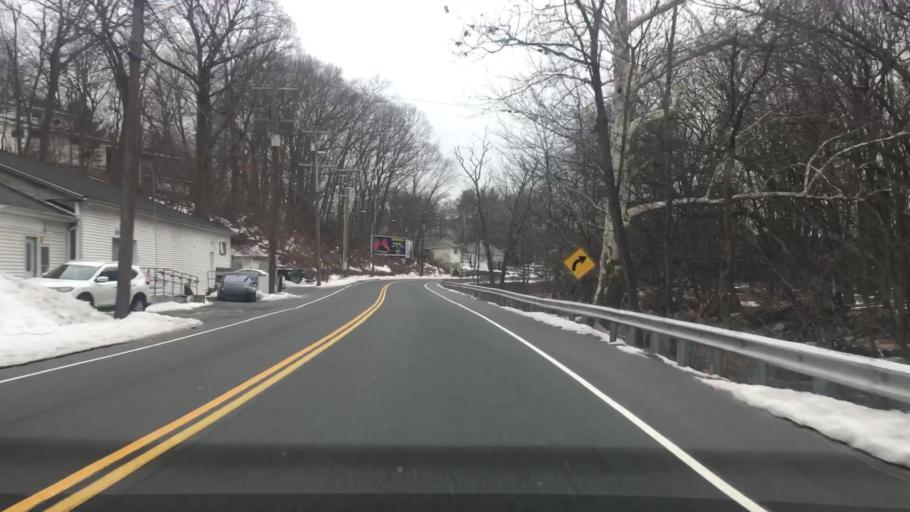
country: US
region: Connecticut
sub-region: Hartford County
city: Plainville
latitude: 41.6727
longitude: -72.9018
